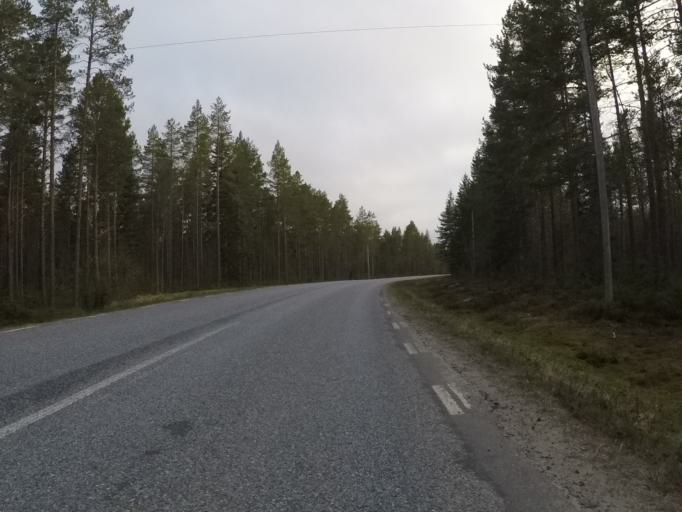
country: SE
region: Vaesterbotten
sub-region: Robertsfors Kommun
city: Robertsfors
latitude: 63.9591
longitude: 20.8070
